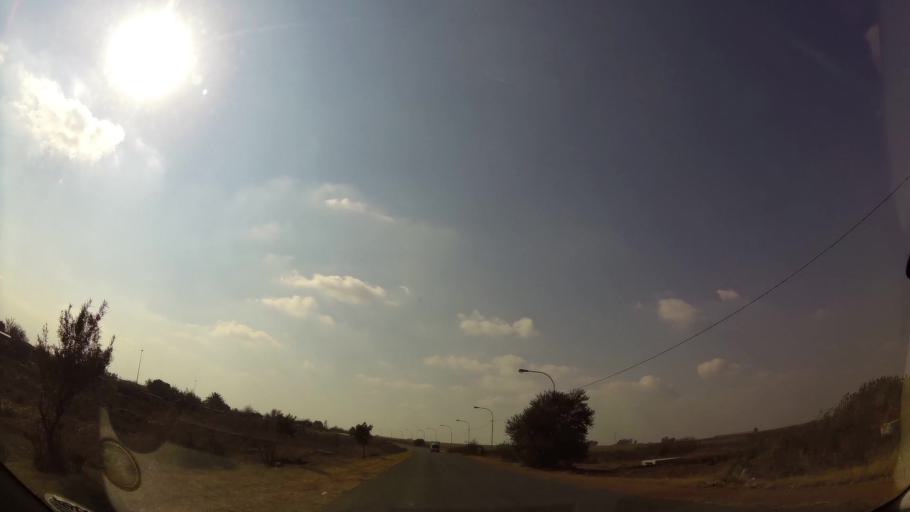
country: ZA
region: Gauteng
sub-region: Ekurhuleni Metropolitan Municipality
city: Springs
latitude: -26.1329
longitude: 28.4802
